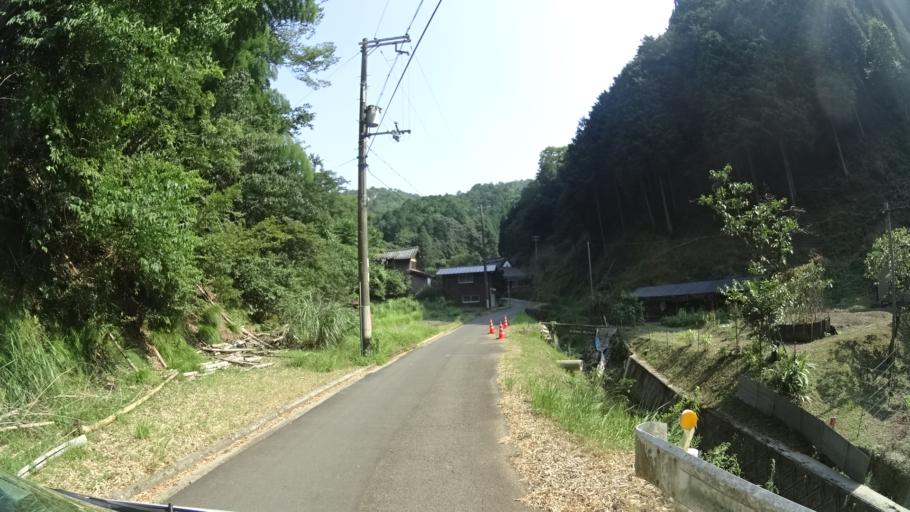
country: JP
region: Kyoto
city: Maizuru
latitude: 35.4025
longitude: 135.2422
